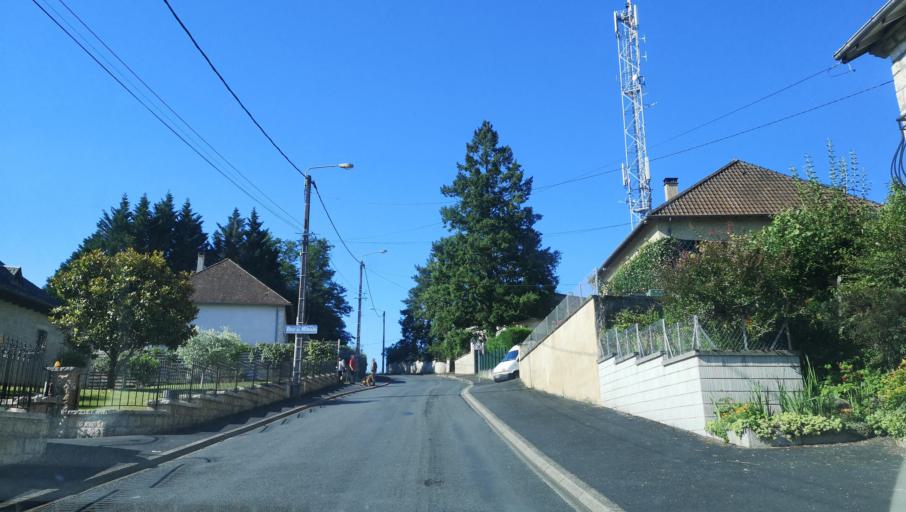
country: FR
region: Limousin
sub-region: Departement de la Correze
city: Brive-la-Gaillarde
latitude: 45.1492
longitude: 1.5495
